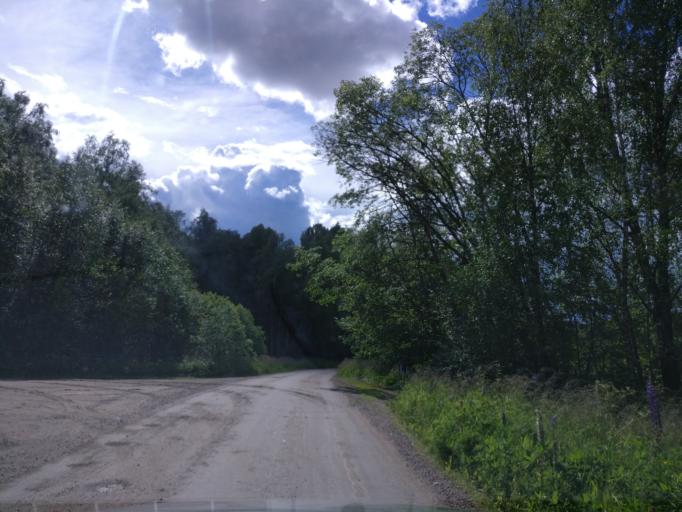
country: SE
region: Vaermland
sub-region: Hagfors Kommun
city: Hagfors
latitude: 60.0388
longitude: 13.6418
